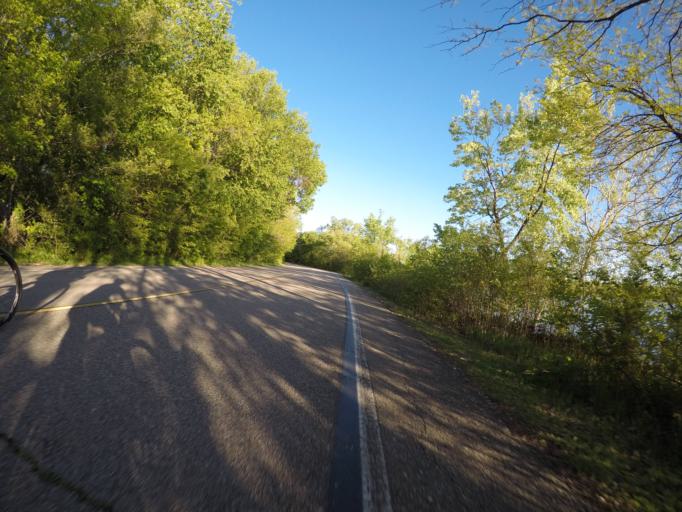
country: US
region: Kansas
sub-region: Riley County
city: Manhattan
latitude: 39.2550
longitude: -96.5762
